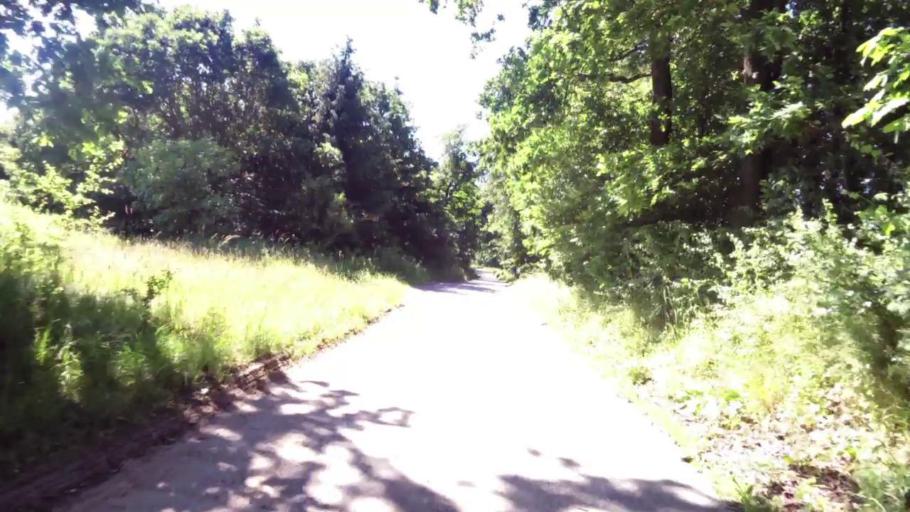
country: PL
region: West Pomeranian Voivodeship
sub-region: Powiat bialogardzki
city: Bialogard
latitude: 53.9265
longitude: 16.0078
